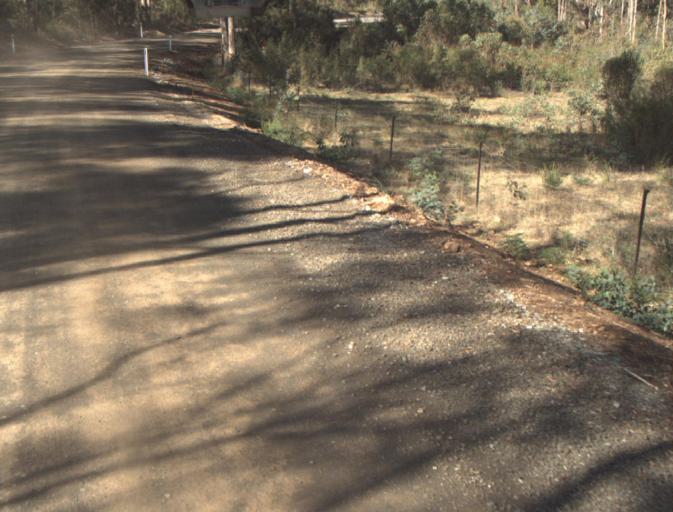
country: AU
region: Tasmania
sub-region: Launceston
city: Mayfield
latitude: -41.2772
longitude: 147.1113
